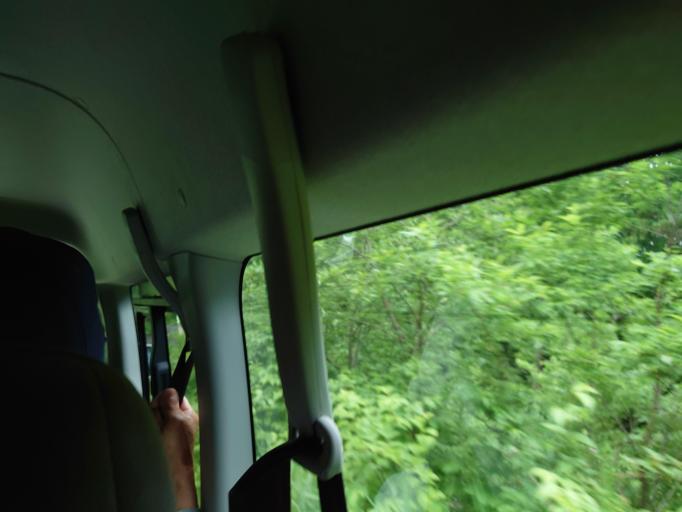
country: JP
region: Iwate
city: Ichinoseki
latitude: 38.9461
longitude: 140.8628
